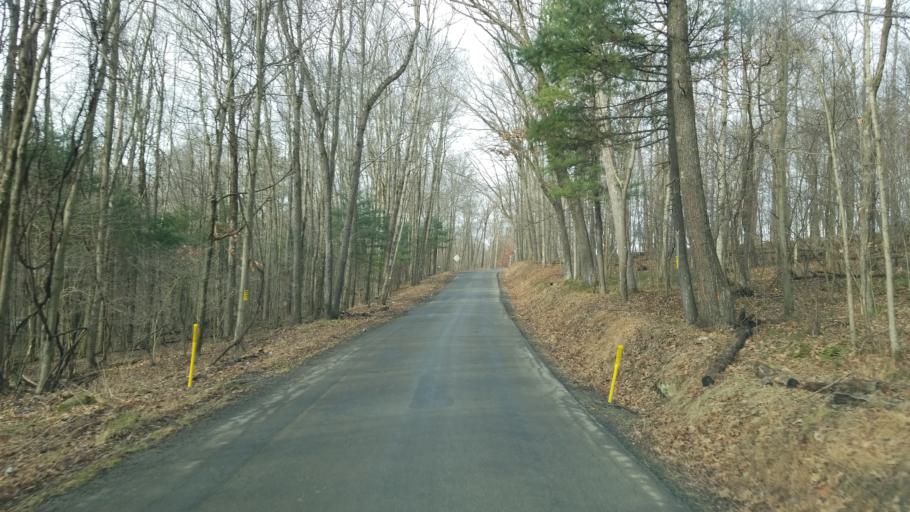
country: US
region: Pennsylvania
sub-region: Jefferson County
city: Punxsutawney
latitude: 40.8518
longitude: -79.0090
